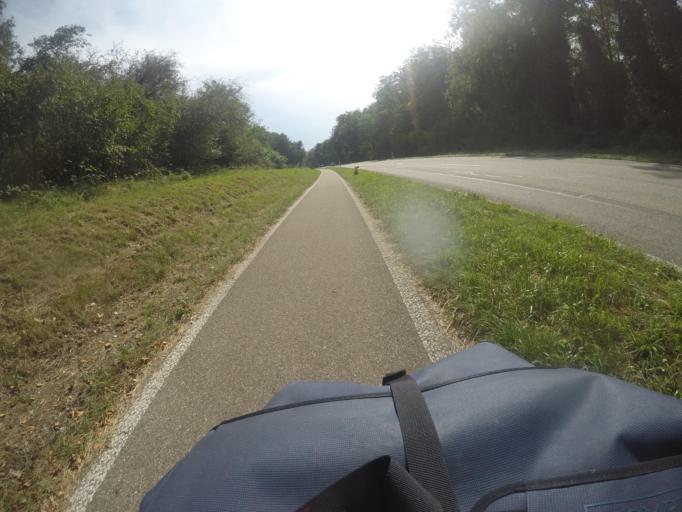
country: FR
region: Alsace
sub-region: Departement du Haut-Rhin
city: Kembs
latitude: 47.6697
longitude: 7.5287
